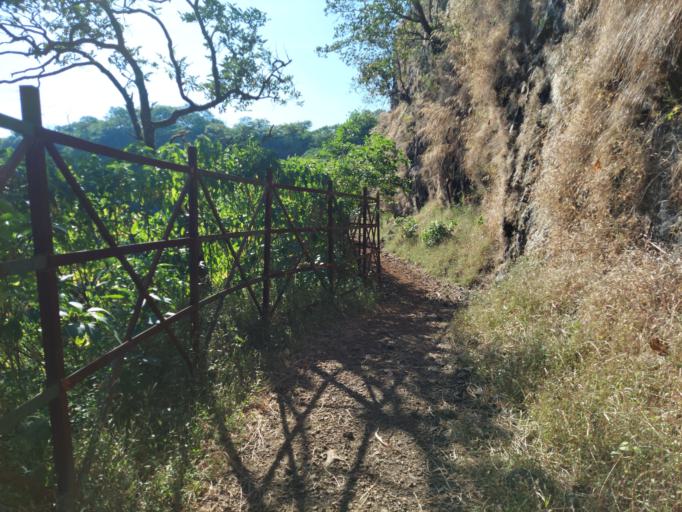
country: IN
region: Maharashtra
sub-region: Sindhudurg
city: Kudal
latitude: 16.0850
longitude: 73.8437
